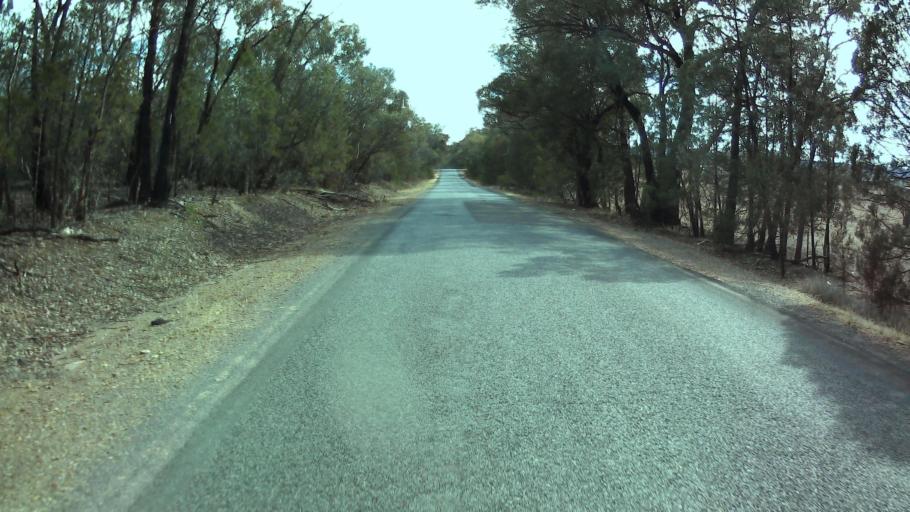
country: AU
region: New South Wales
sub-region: Weddin
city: Grenfell
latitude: -33.8935
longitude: 148.1891
